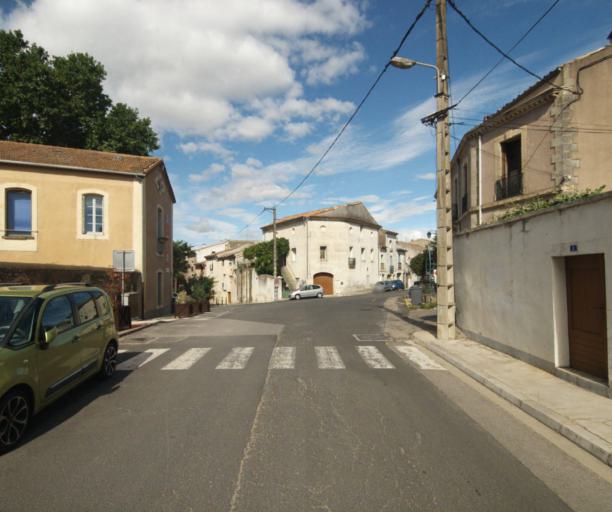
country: FR
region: Languedoc-Roussillon
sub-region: Departement de l'Herault
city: Aniane
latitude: 43.6845
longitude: 3.5904
